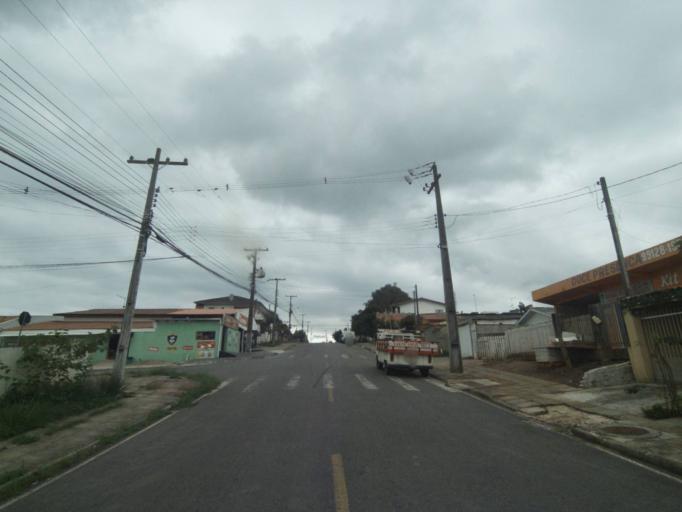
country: BR
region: Parana
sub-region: Quatro Barras
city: Quatro Barras
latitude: -25.3519
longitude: -49.1109
